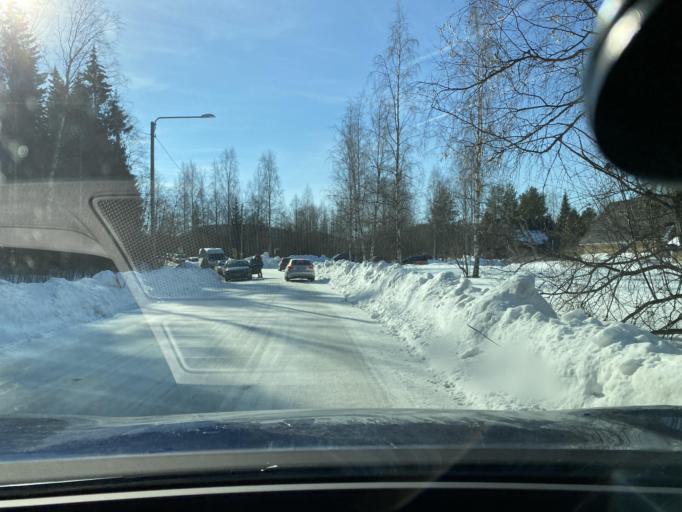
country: FI
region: Central Finland
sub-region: Jyvaeskylae
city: Muurame
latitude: 62.0936
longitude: 25.6430
